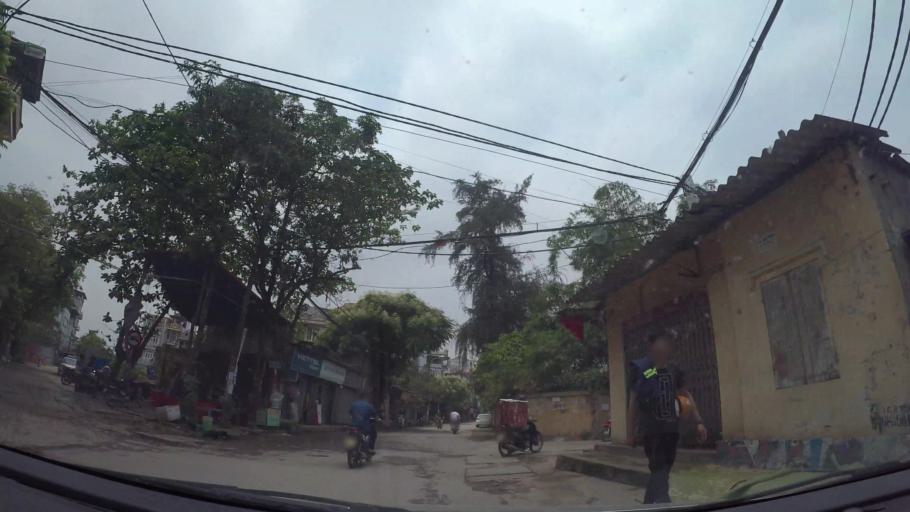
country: VN
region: Ha Noi
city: Tay Ho
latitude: 21.0761
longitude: 105.7882
